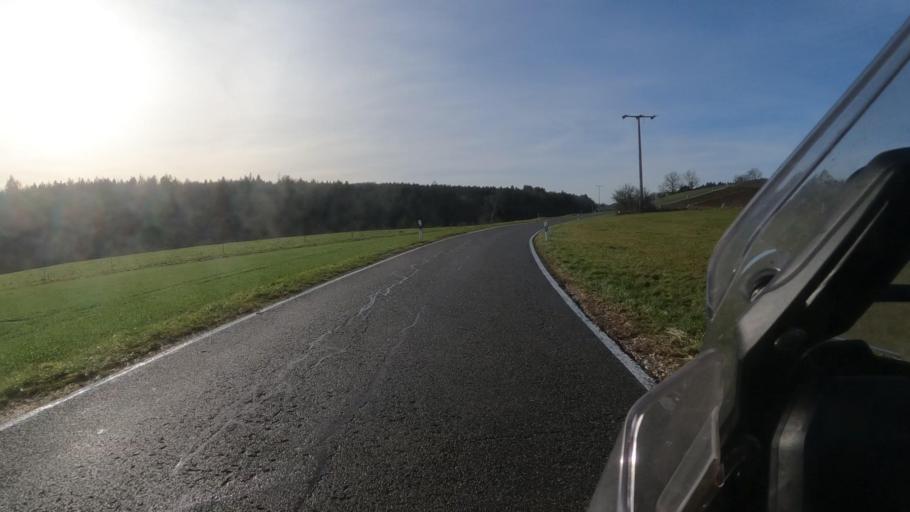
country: DE
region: Baden-Wuerttemberg
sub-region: Freiburg Region
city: Tengen
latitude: 47.8027
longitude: 8.6597
